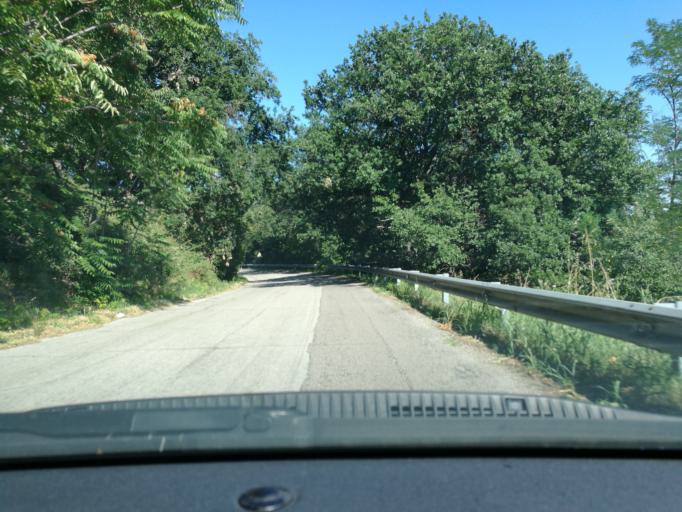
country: IT
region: Abruzzo
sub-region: Provincia di Chieti
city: Vasto
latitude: 42.1662
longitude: 14.6959
